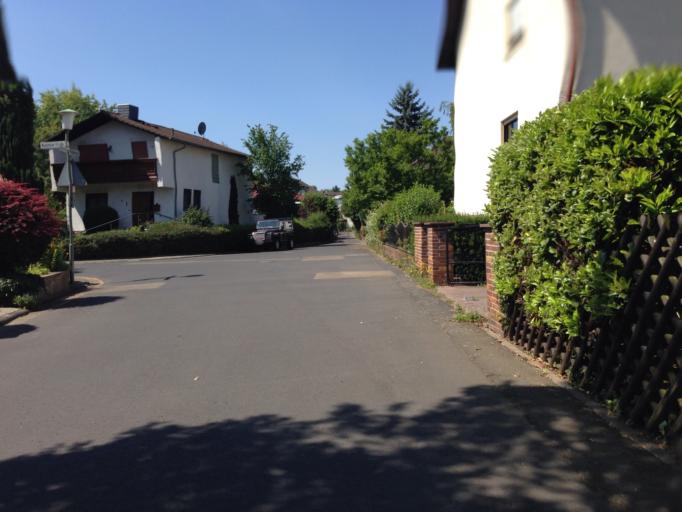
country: DE
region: Hesse
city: Bruchkobel
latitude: 50.1757
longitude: 8.8860
